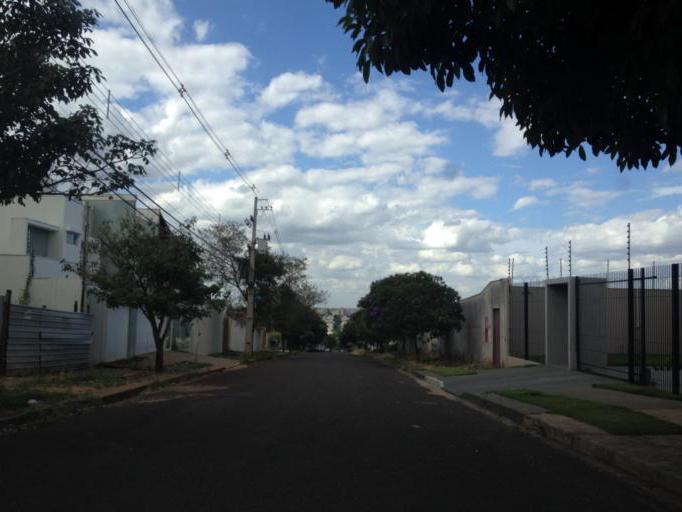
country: BR
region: Parana
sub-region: Maringa
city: Maringa
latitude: -23.4468
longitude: -51.9503
